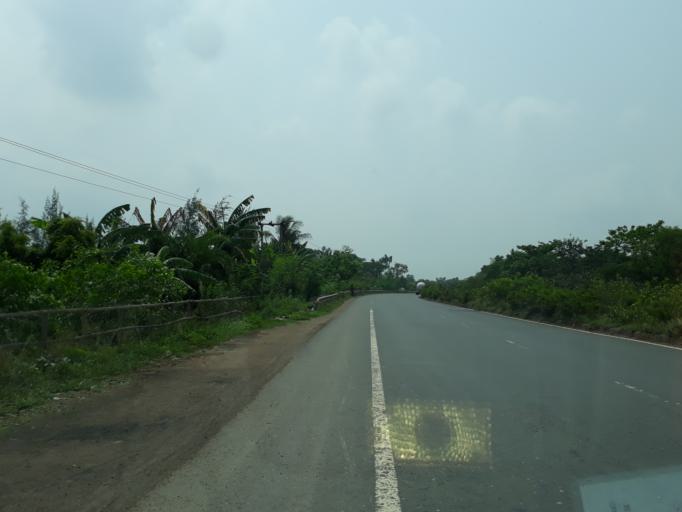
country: IN
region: West Bengal
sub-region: Purba Medinipur
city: Mahishadal
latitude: 22.1522
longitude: 87.9576
